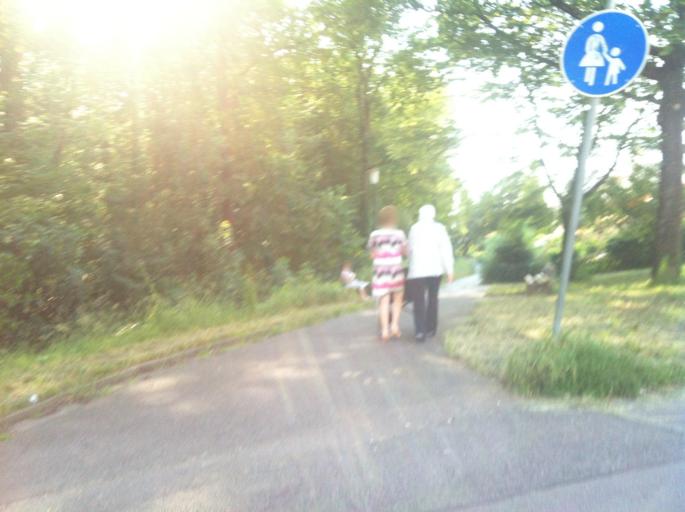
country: DE
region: Baden-Wuerttemberg
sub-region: Karlsruhe Region
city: Leimen
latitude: 49.3705
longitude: 8.7054
